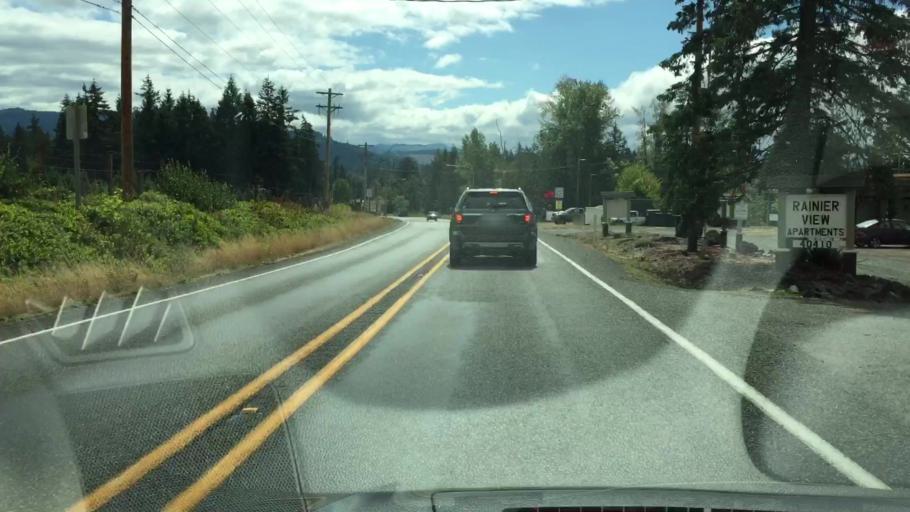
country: US
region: Washington
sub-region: Pierce County
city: Eatonville
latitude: 46.8888
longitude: -122.3001
